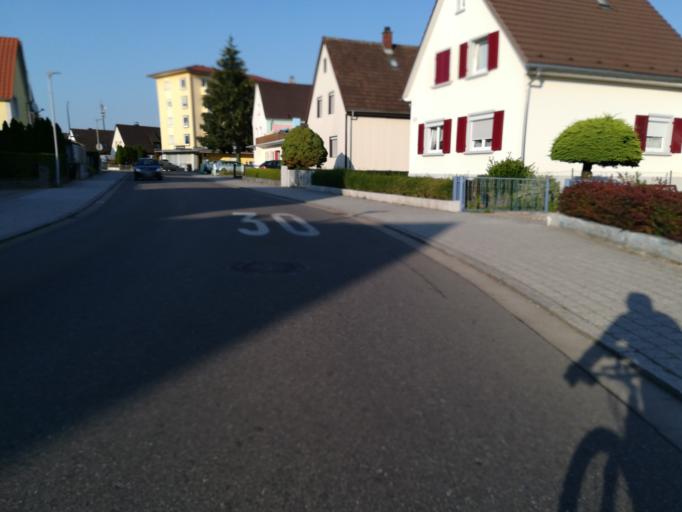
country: DE
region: Baden-Wuerttemberg
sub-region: Freiburg Region
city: Rielasingen-Worblingen
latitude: 47.7461
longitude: 8.8459
